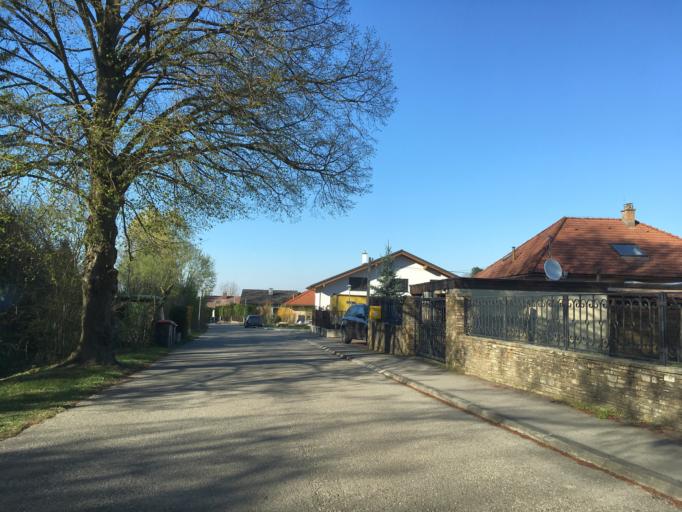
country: AT
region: Lower Austria
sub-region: Politischer Bezirk Tulln
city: Konigstetten
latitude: 48.2994
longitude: 16.1571
